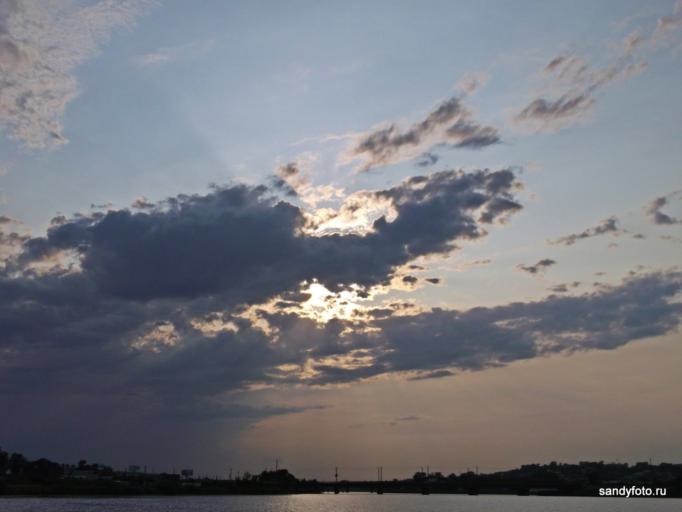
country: RU
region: Chelyabinsk
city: Troitsk
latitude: 54.0895
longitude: 61.5819
